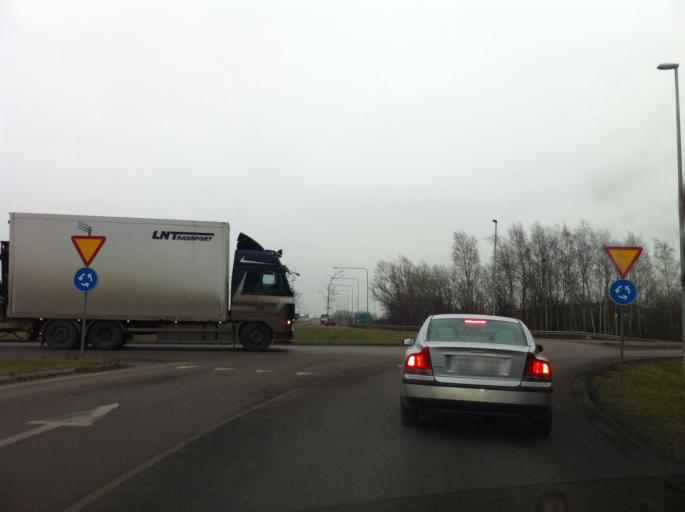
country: SE
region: Skane
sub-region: Landskrona
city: Landskrona
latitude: 55.8737
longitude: 12.8670
